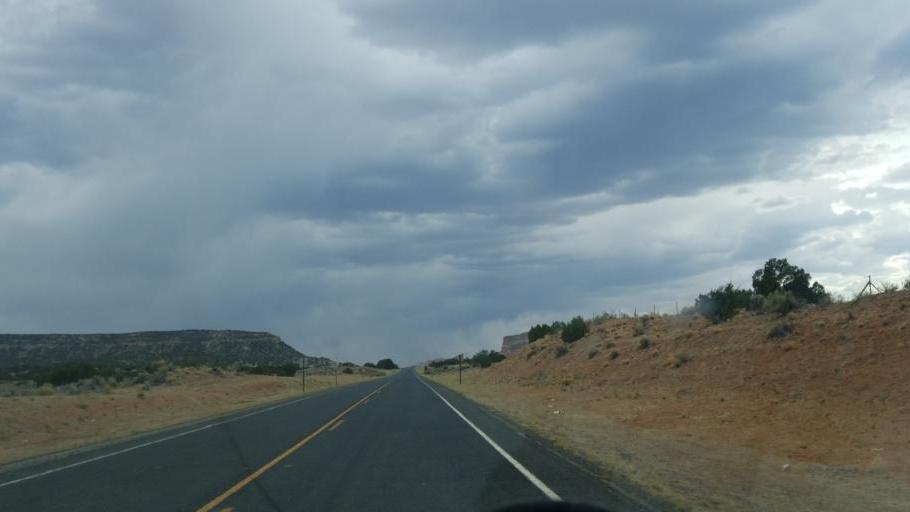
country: US
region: Arizona
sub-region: Apache County
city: Houck
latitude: 35.3785
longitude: -109.0221
